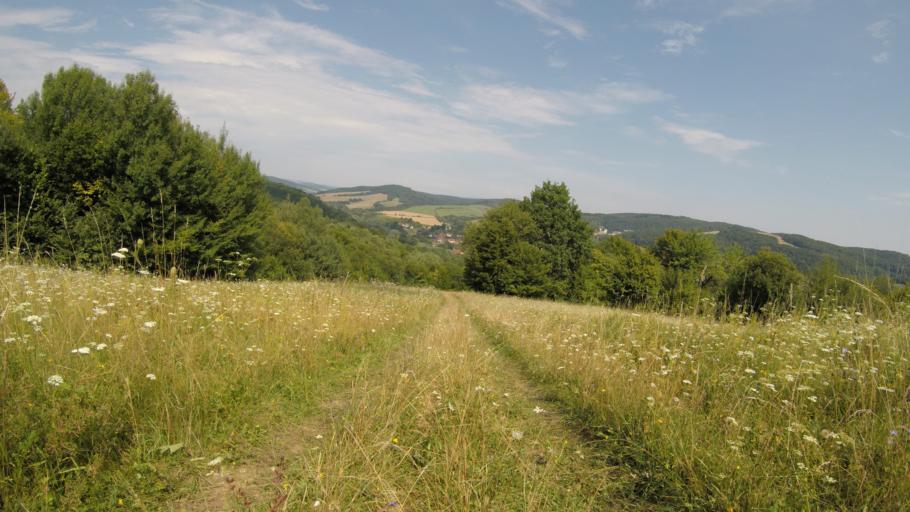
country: SK
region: Presovsky
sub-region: Okres Presov
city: Presov
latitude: 48.9398
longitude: 21.1672
